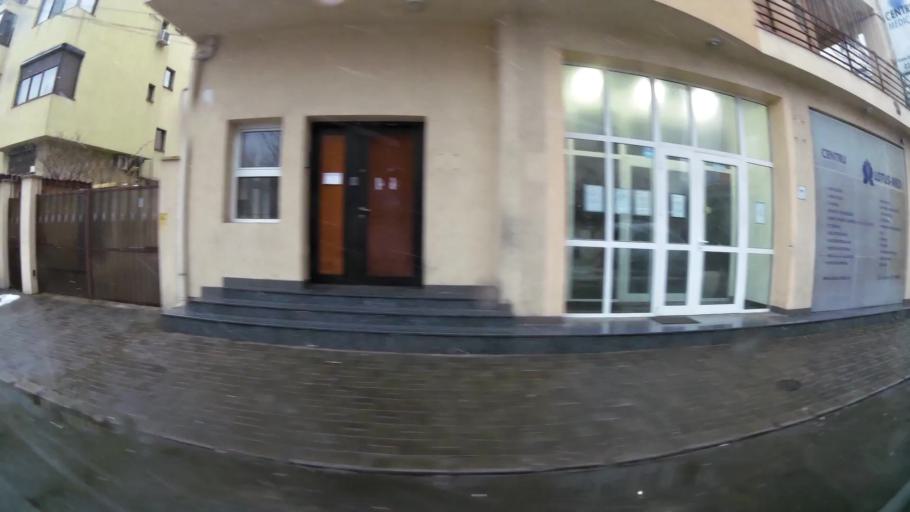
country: RO
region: Ilfov
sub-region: Comuna Chiajna
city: Rosu
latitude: 44.4717
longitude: 26.0486
